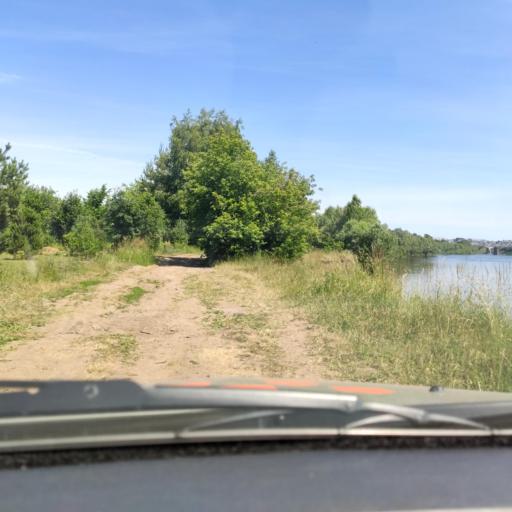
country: RU
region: Bashkortostan
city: Iglino
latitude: 54.7830
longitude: 56.1923
